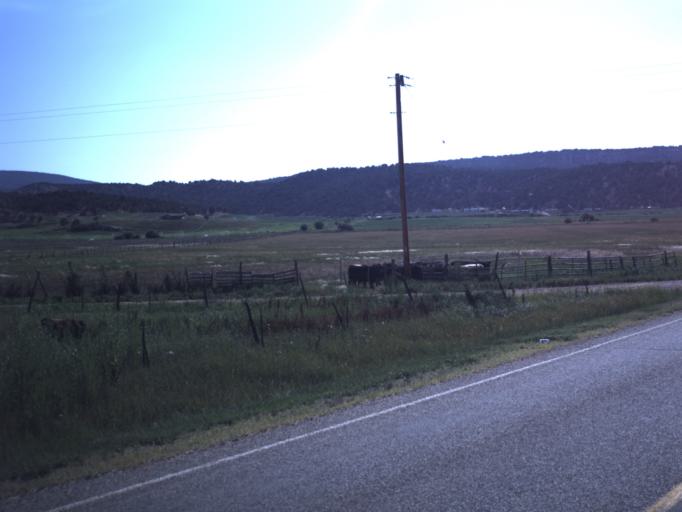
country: US
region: Utah
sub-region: Duchesne County
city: Duchesne
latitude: 40.3382
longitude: -110.6857
